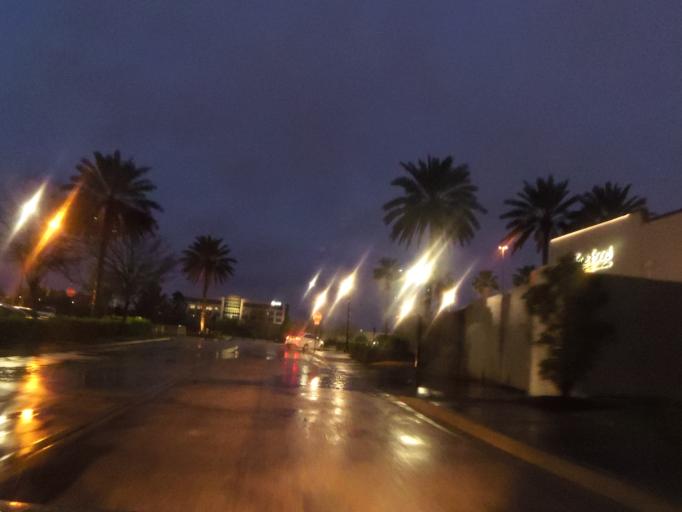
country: US
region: Florida
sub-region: Duval County
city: Jacksonville Beach
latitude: 30.2528
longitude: -81.5247
